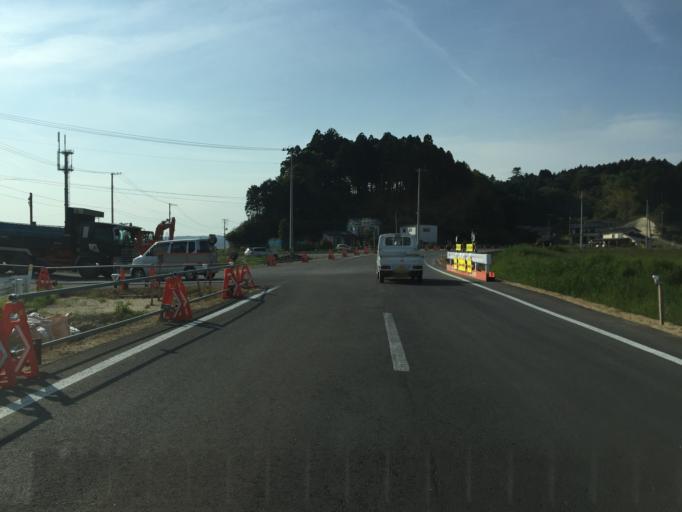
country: JP
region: Fukushima
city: Namie
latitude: 37.7269
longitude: 141.0048
